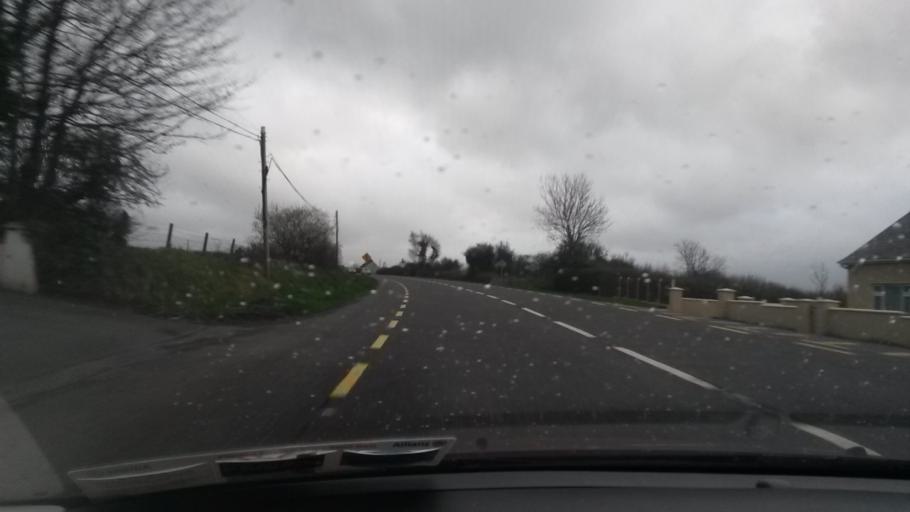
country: IE
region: Munster
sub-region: County Limerick
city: Abbeyfeale
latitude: 52.3638
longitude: -9.3247
